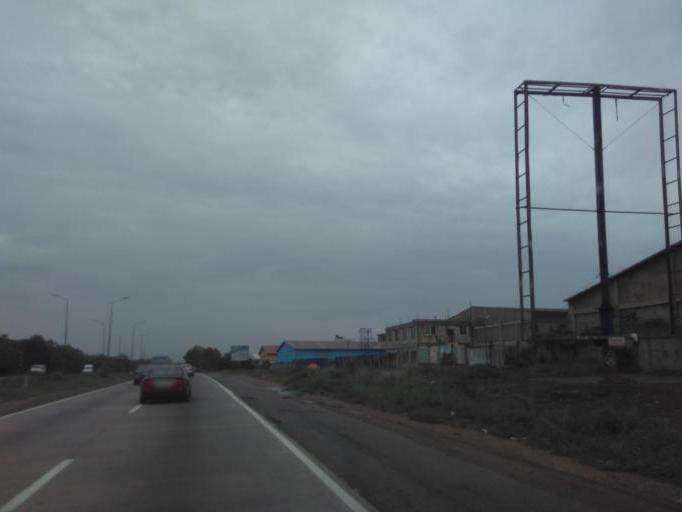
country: GH
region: Greater Accra
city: Medina Estates
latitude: 5.6308
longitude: -0.1523
